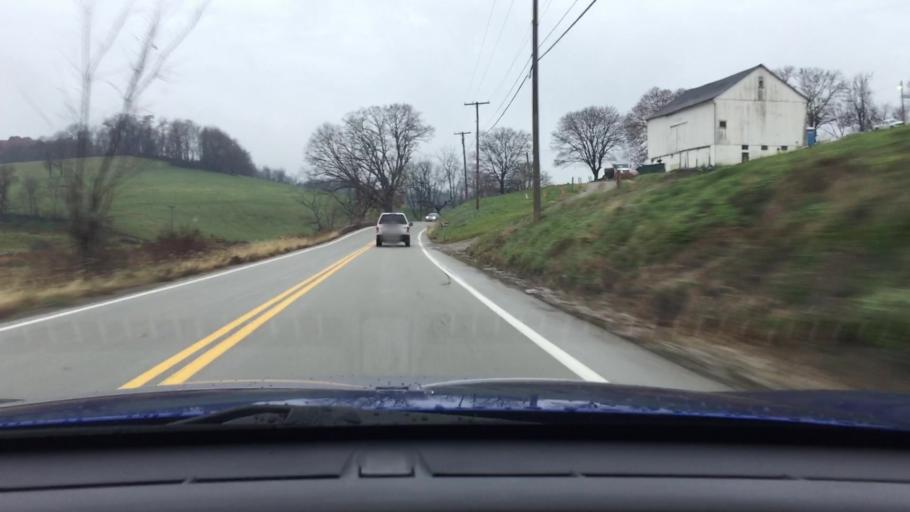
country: US
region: Pennsylvania
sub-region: Washington County
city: Ellsworth
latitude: 40.1759
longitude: -80.0938
